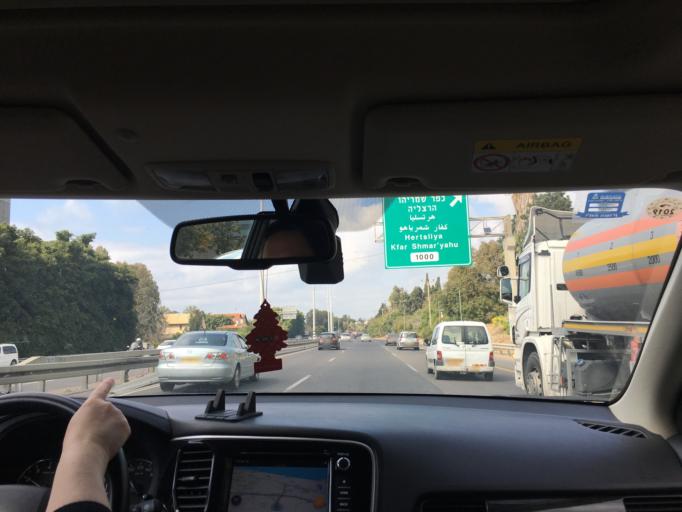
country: IL
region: Tel Aviv
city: Herzliyya
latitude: 32.1677
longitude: 34.8138
